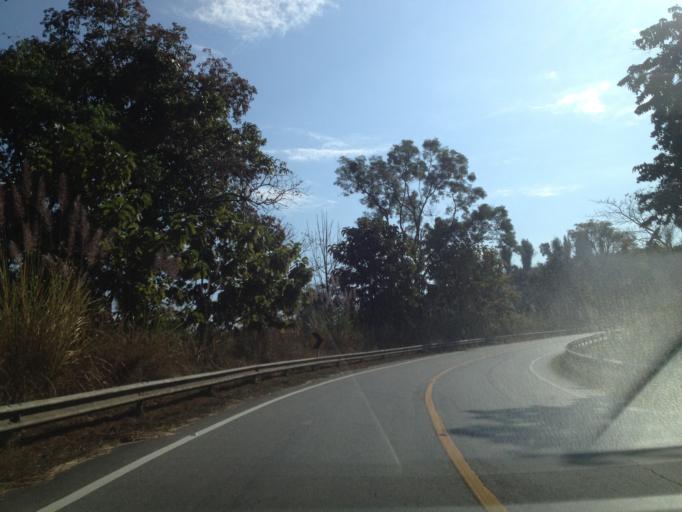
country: TH
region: Mae Hong Son
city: Pa Pae
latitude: 18.1671
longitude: 98.2304
